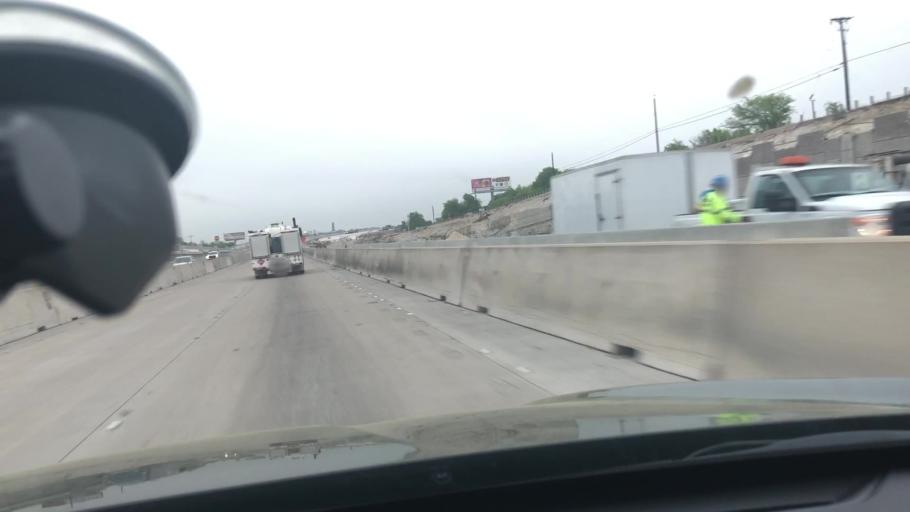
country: US
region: Texas
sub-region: Bell County
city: Temple
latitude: 31.1146
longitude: -97.3552
